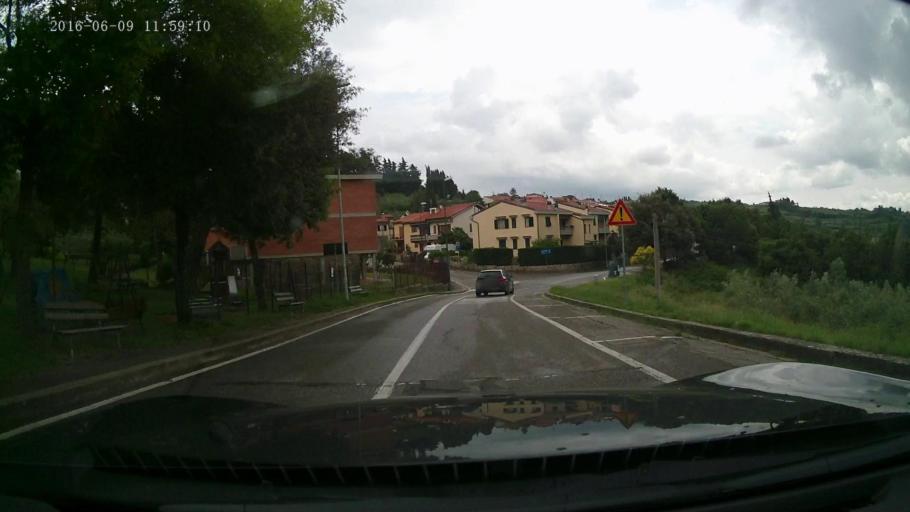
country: IT
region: Tuscany
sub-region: Province of Florence
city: Panzano in Chianti
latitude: 43.5451
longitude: 11.3113
